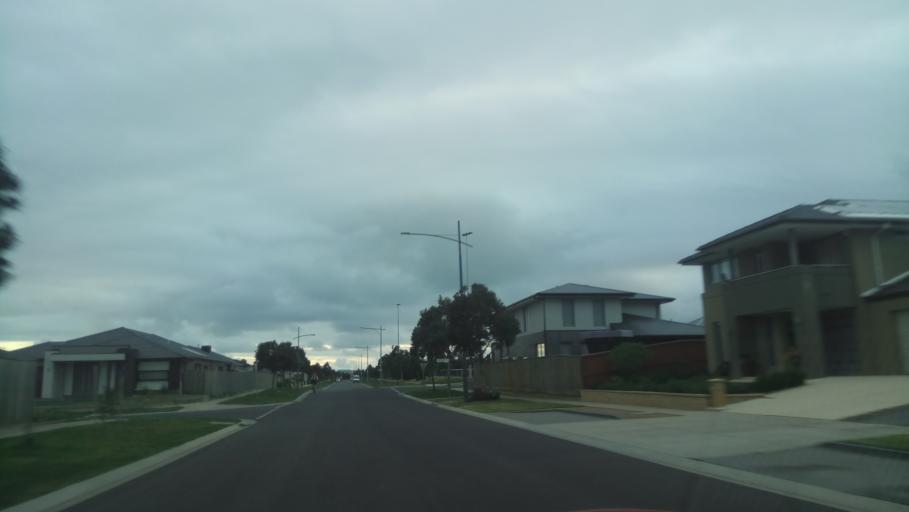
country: AU
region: Victoria
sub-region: Wyndham
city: Point Cook
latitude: -37.9062
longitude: 144.7591
